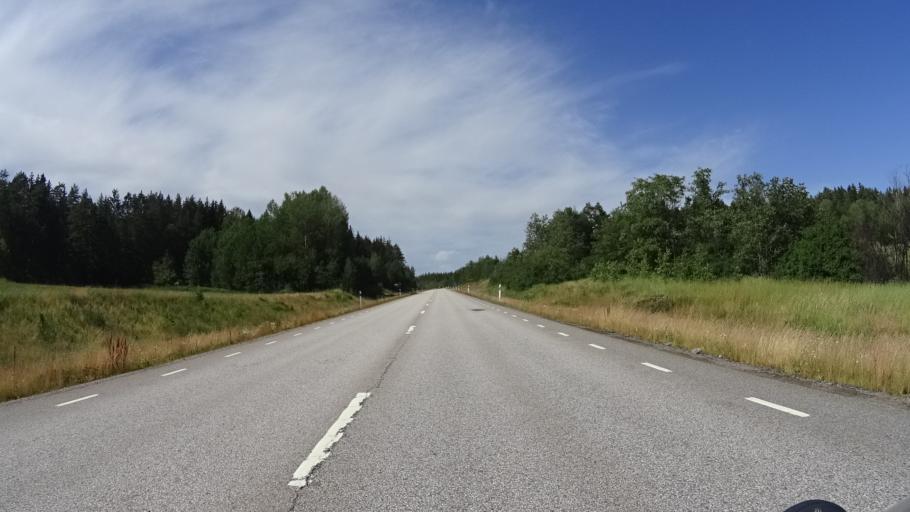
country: SE
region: Kalmar
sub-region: Vasterviks Kommun
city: Gamleby
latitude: 57.9494
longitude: 16.3800
